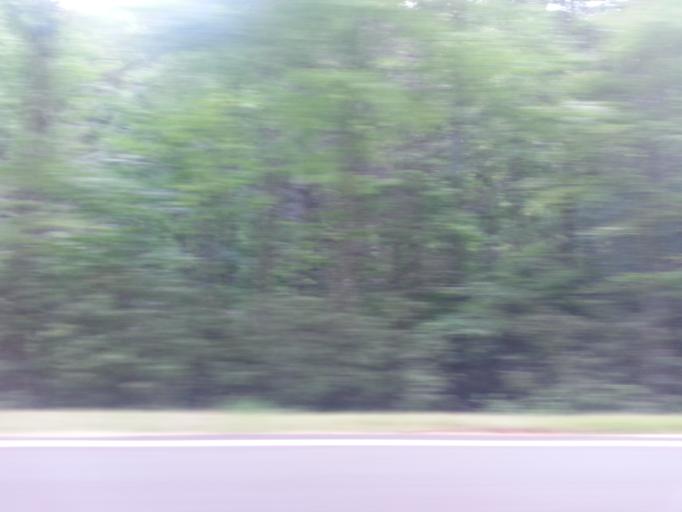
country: US
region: Georgia
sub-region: Towns County
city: Hiawassee
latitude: 34.8328
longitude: -83.7638
